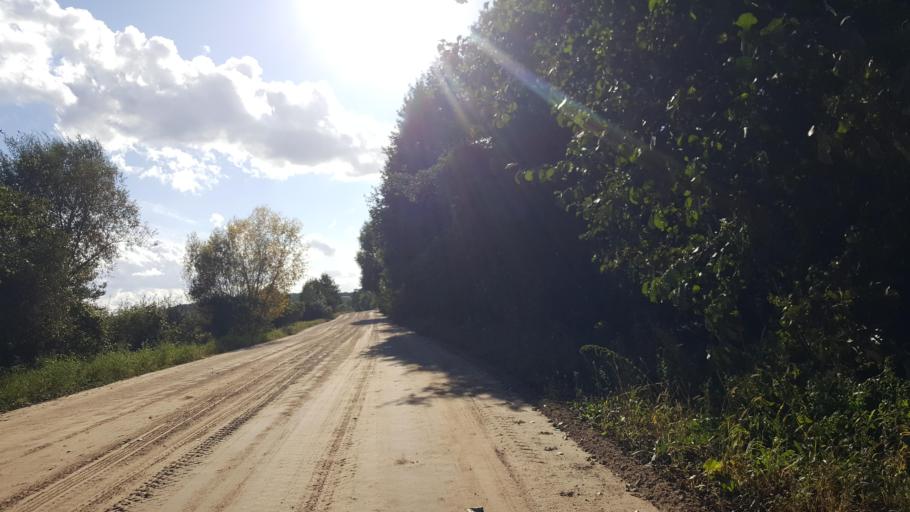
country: BY
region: Brest
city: Kamyanyets
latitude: 52.4216
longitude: 23.9382
